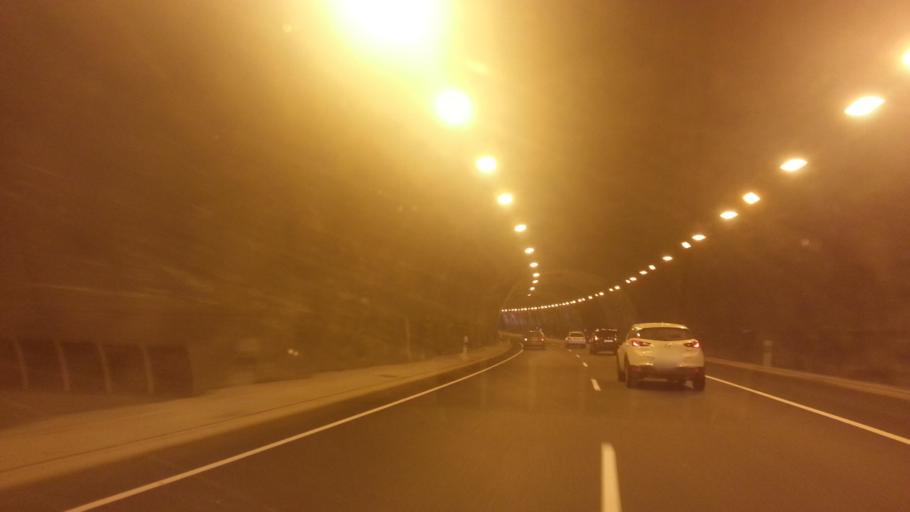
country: ES
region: Catalonia
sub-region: Provincia de Barcelona
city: Sant Pere de Ribes
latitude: 41.2994
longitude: 1.7270
